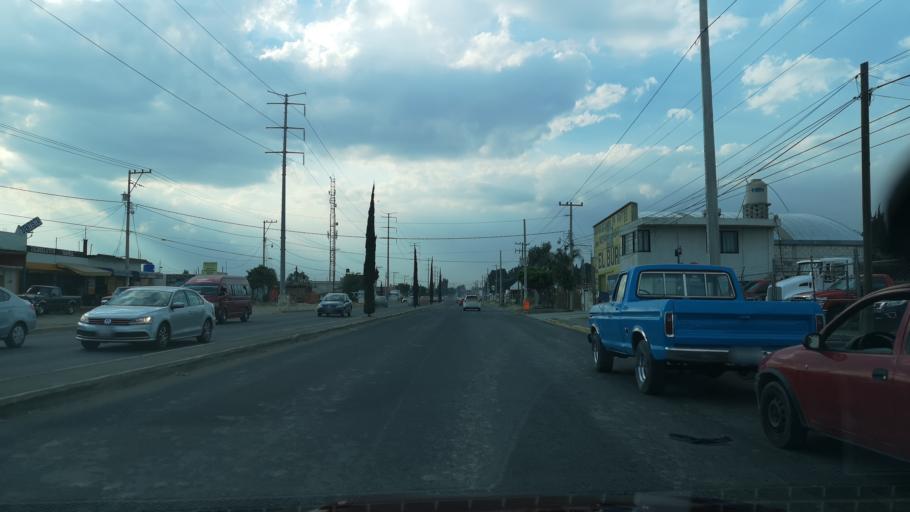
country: MX
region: Puebla
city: Cuanala
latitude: 19.0869
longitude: -98.3329
